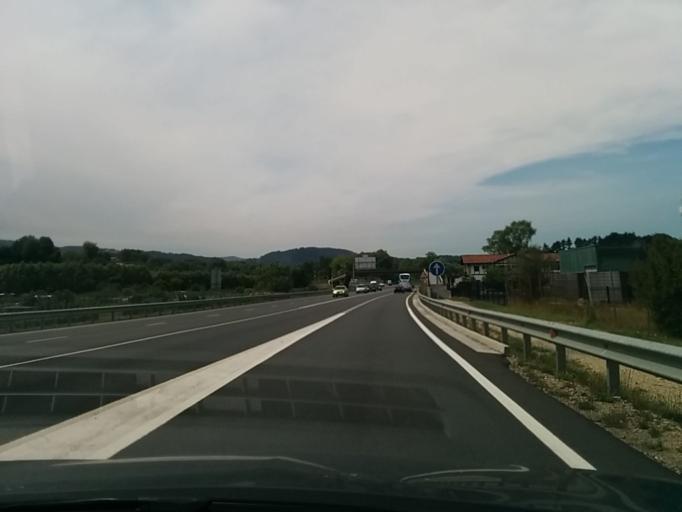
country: ES
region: Basque Country
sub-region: Provincia de Guipuzcoa
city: Irun
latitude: 43.3459
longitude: -1.8145
